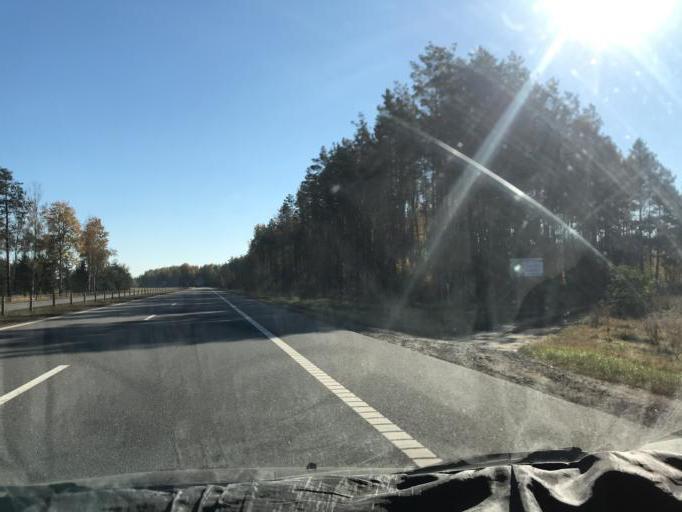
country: BY
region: Mogilev
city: Babruysk
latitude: 53.2125
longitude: 29.0479
